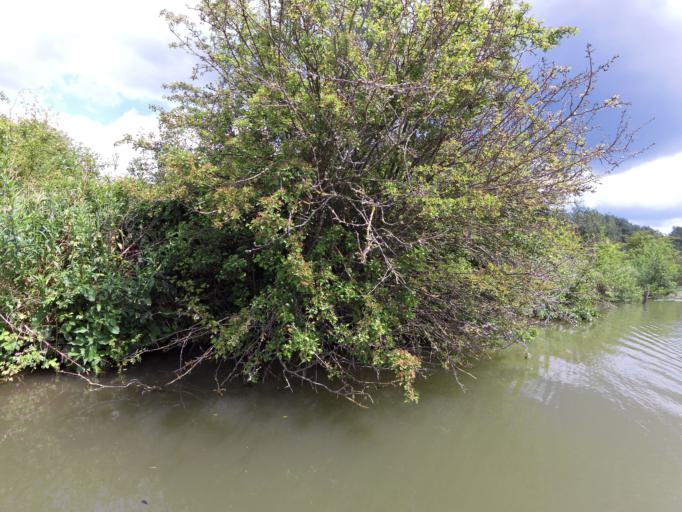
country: FR
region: Nord-Pas-de-Calais
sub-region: Departement du Pas-de-Calais
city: Saint-Omer
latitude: 50.7663
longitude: 2.2500
